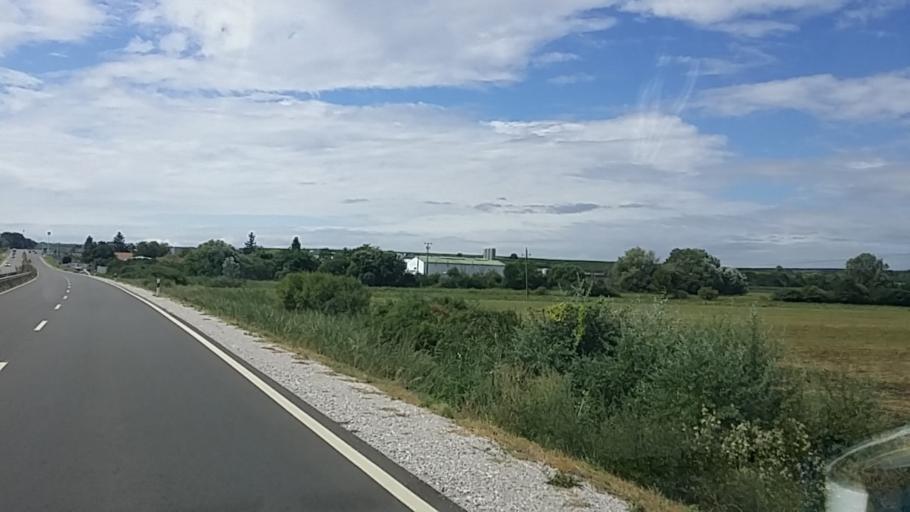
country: HU
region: Heves
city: Nagyrede
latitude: 47.7464
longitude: 19.8773
